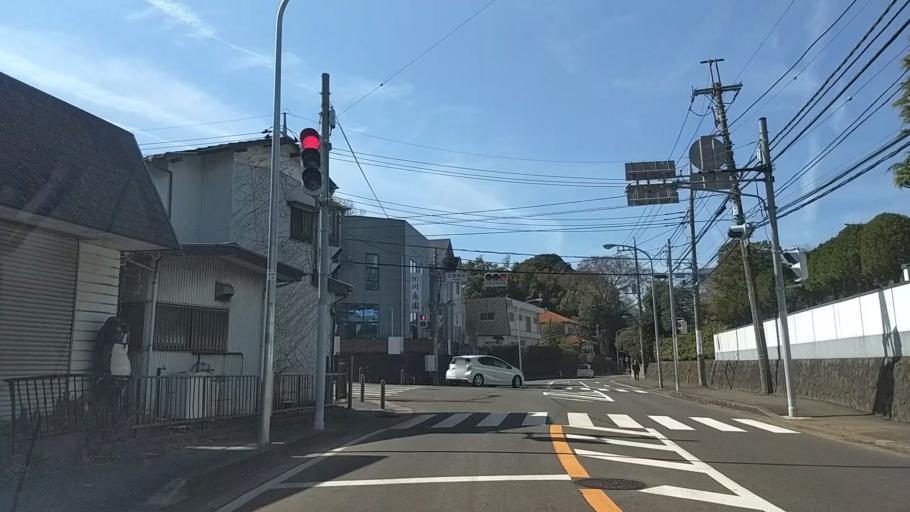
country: JP
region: Kanagawa
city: Fujisawa
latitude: 35.3909
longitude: 139.5137
